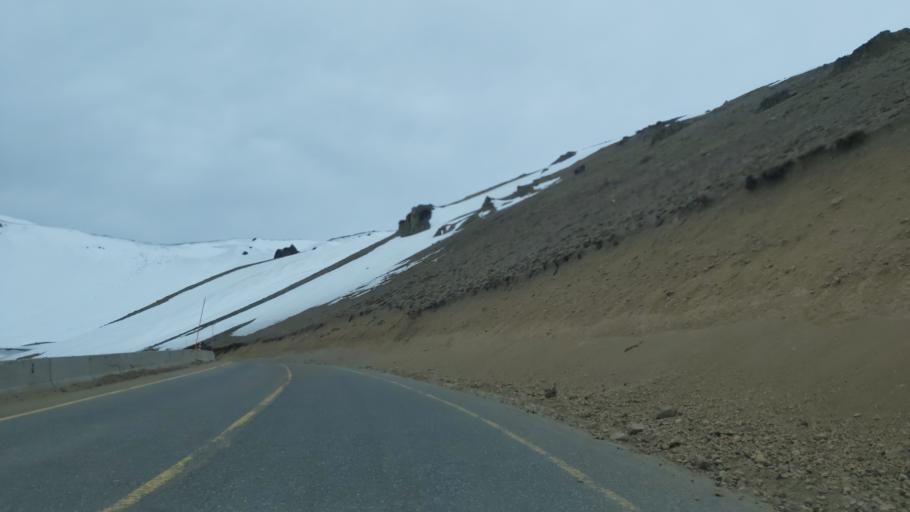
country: CL
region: Maule
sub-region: Provincia de Linares
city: Colbun
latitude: -36.0205
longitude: -70.5032
